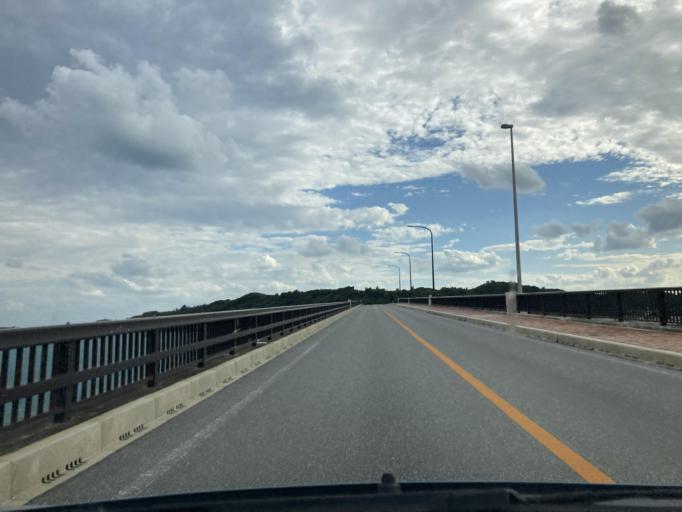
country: JP
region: Okinawa
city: Katsuren-haebaru
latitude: 26.3344
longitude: 127.9558
